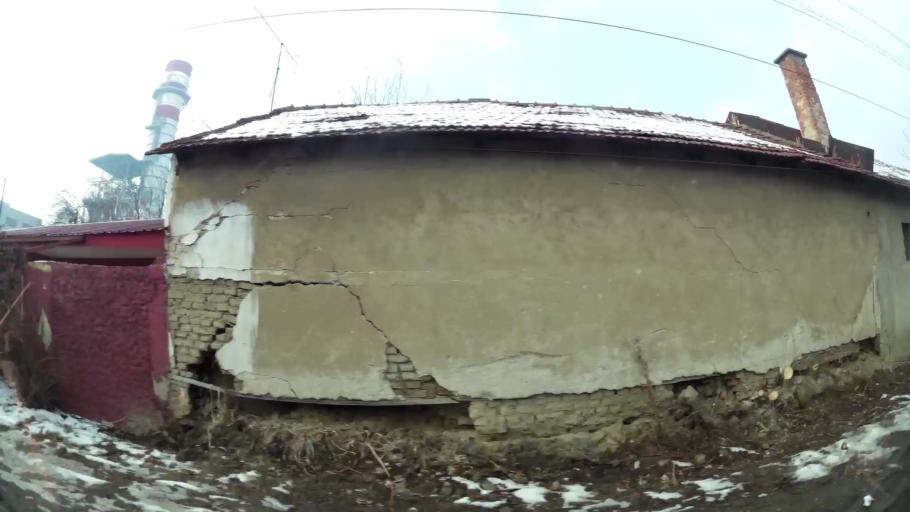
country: MK
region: Karpos
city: Skopje
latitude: 41.9950
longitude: 21.4539
